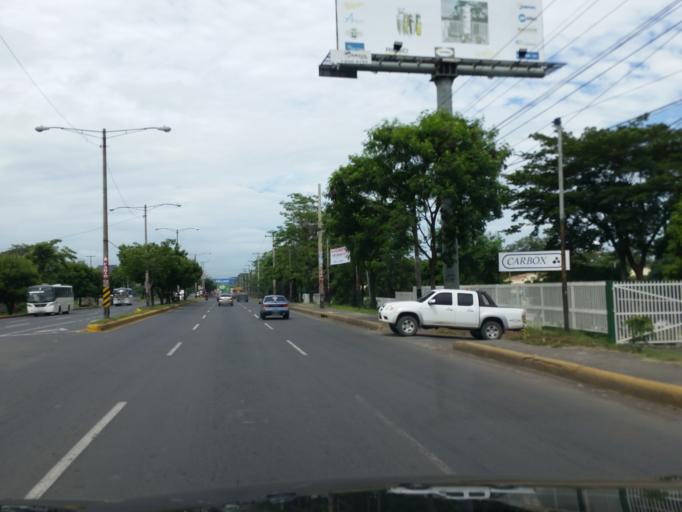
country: NI
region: Managua
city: Managua
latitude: 12.1489
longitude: -86.2038
